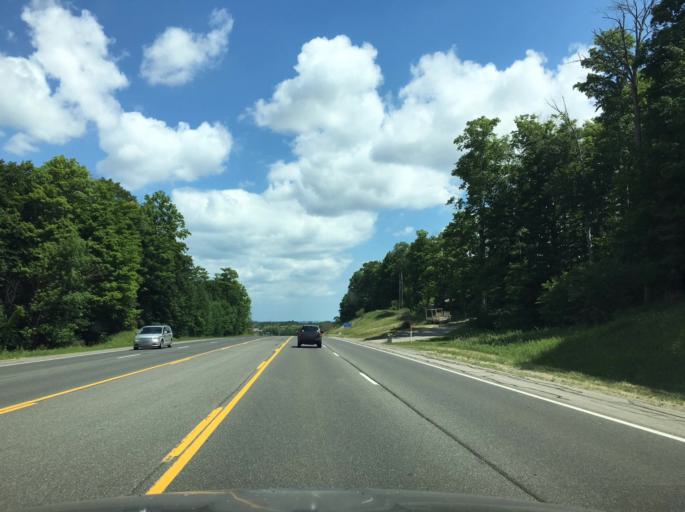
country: US
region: Michigan
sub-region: Grand Traverse County
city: Traverse City
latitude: 44.7126
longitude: -85.6493
